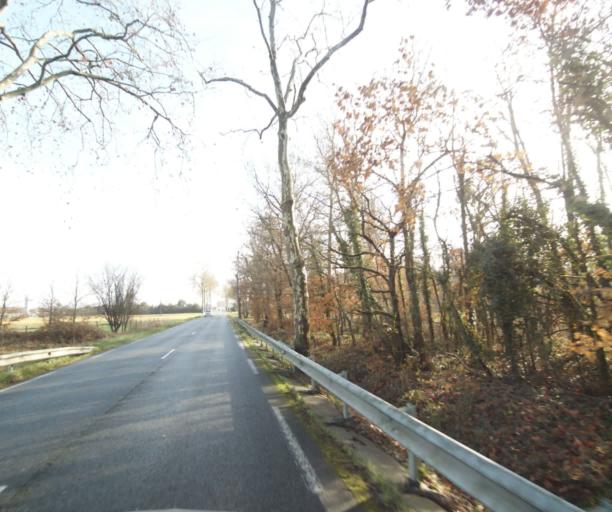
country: FR
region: Midi-Pyrenees
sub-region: Departement du Tarn-et-Garonne
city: Nohic
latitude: 43.8771
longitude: 1.4554
